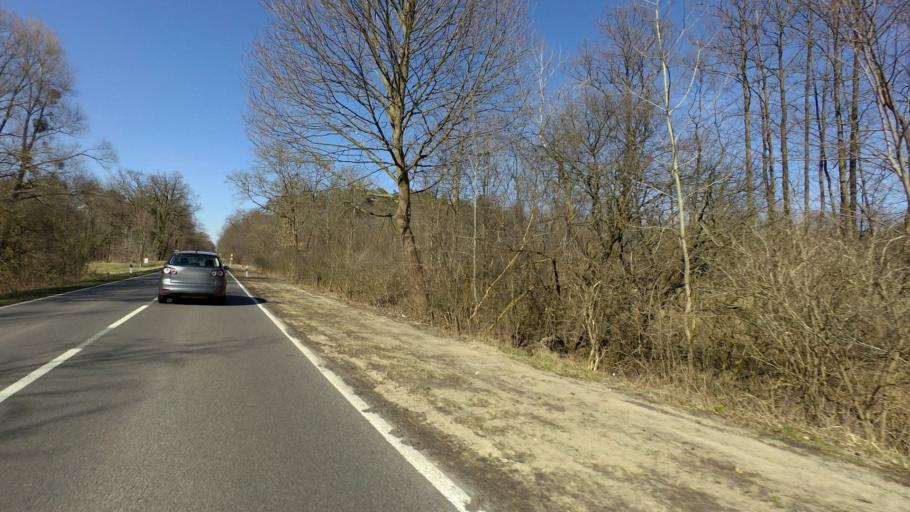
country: DE
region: Brandenburg
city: Eberswalde
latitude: 52.8148
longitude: 13.8333
